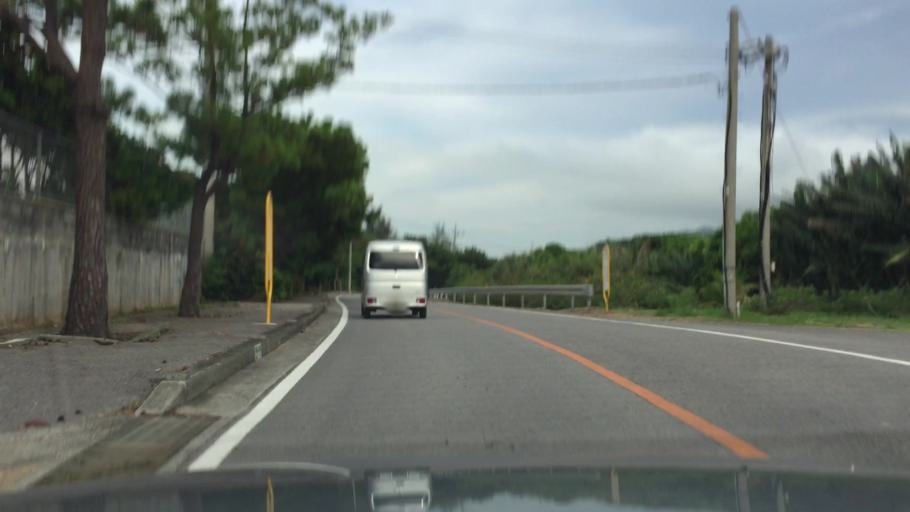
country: JP
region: Okinawa
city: Ishigaki
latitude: 24.4055
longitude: 124.1455
